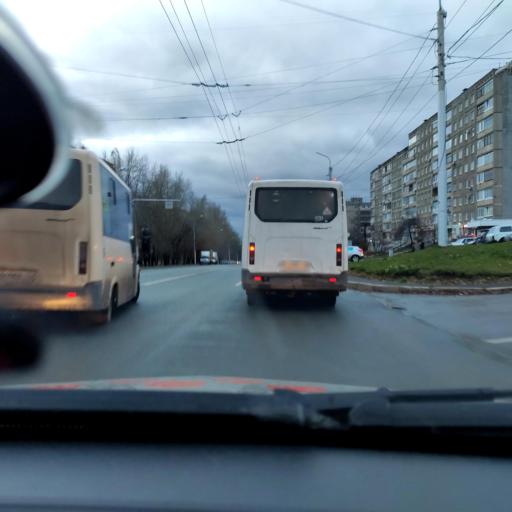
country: RU
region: Bashkortostan
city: Ufa
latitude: 54.7043
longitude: 55.9973
